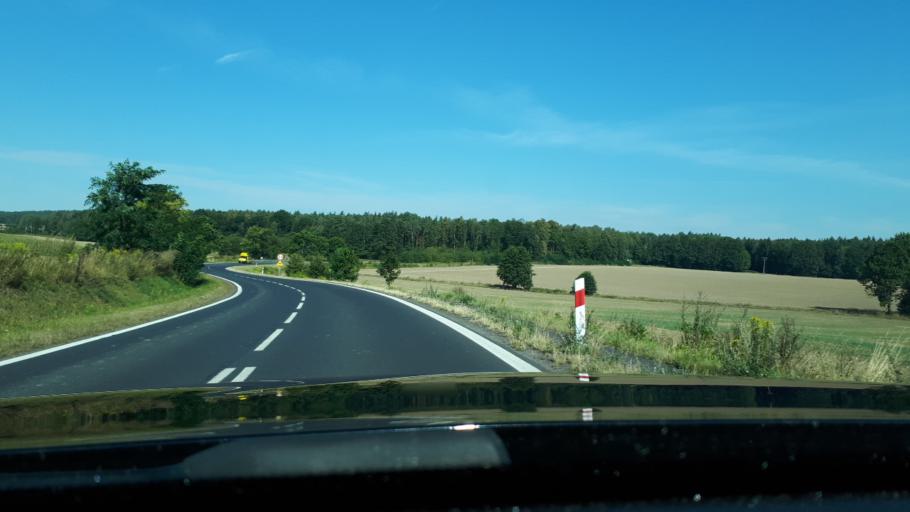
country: PL
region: Lower Silesian Voivodeship
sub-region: Powiat lubanski
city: Pisarzowice
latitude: 51.1822
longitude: 15.2555
